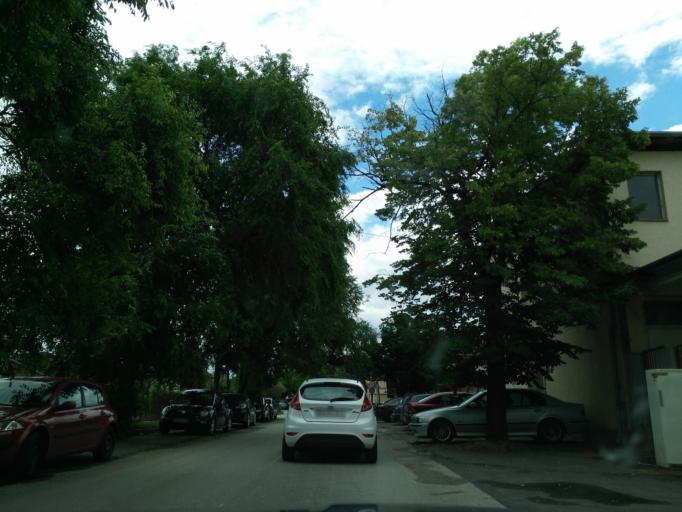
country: HU
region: Hajdu-Bihar
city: Debrecen
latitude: 47.5419
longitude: 21.6428
